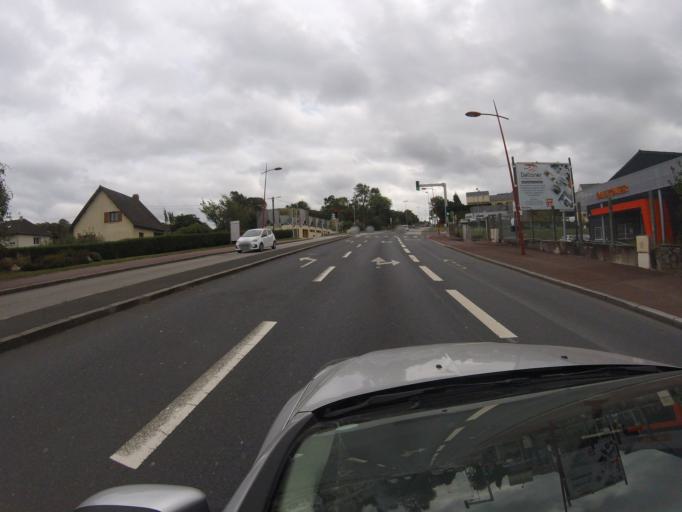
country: FR
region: Lower Normandy
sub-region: Departement de la Manche
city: La Glacerie
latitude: 49.6126
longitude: -1.6013
